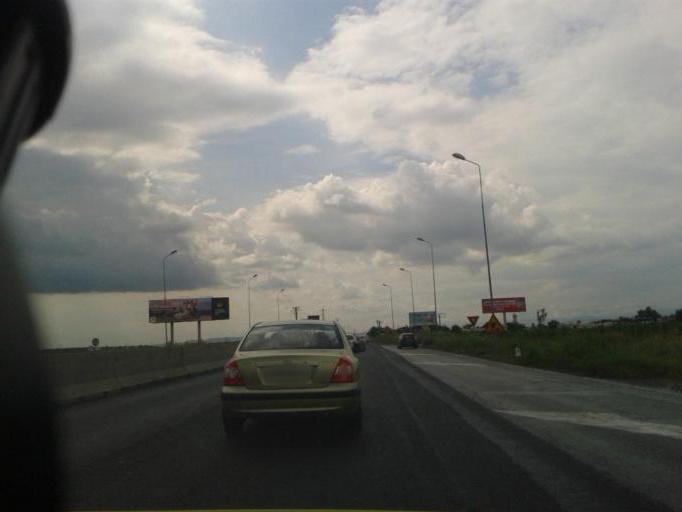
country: RO
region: Prahova
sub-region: Comuna Paulesti
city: Paulesti
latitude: 44.9724
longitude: 25.9534
